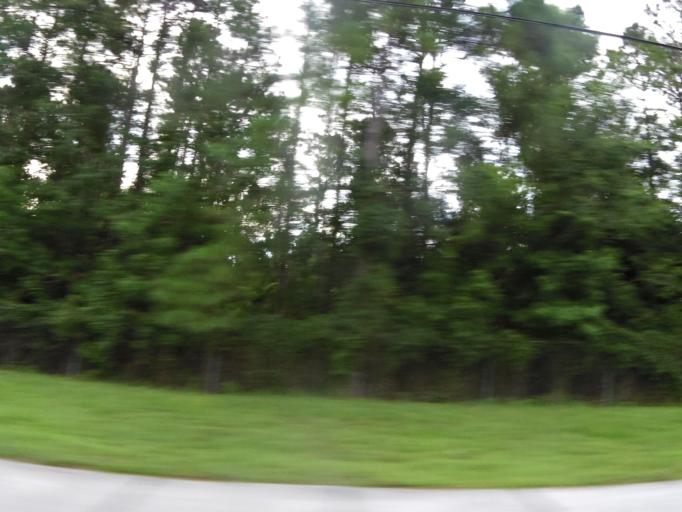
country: US
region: Florida
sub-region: Clay County
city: Bellair-Meadowbrook Terrace
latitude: 30.3021
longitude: -81.8242
